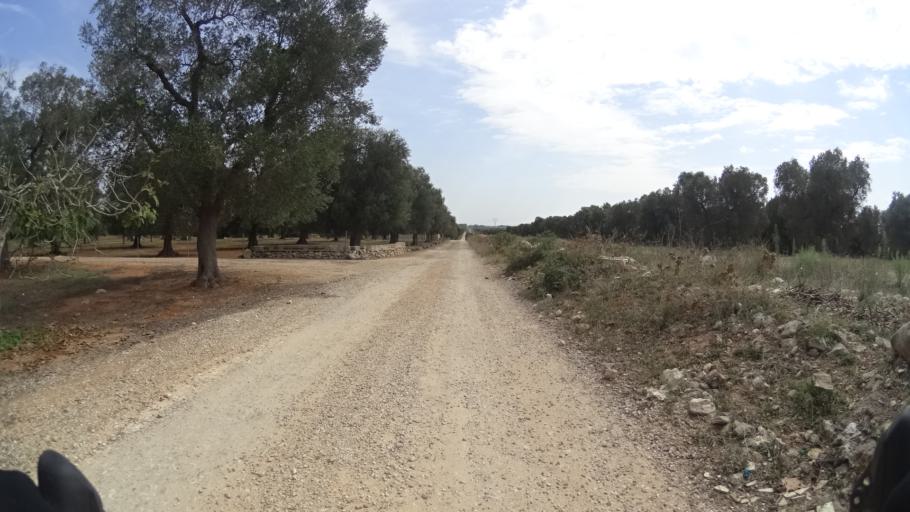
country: IT
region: Apulia
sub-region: Provincia di Lecce
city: Porto Cesareo
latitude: 40.2963
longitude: 17.9183
